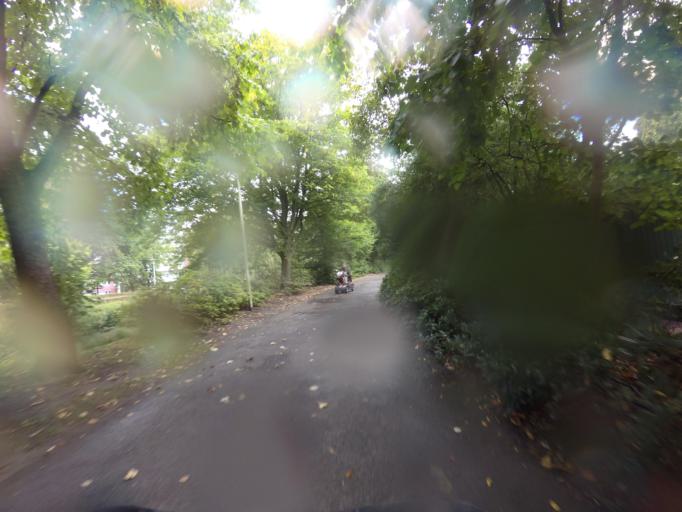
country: DE
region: North Rhine-Westphalia
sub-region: Regierungsbezirk Munster
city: Gronau
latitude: 52.2069
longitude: 7.0210
